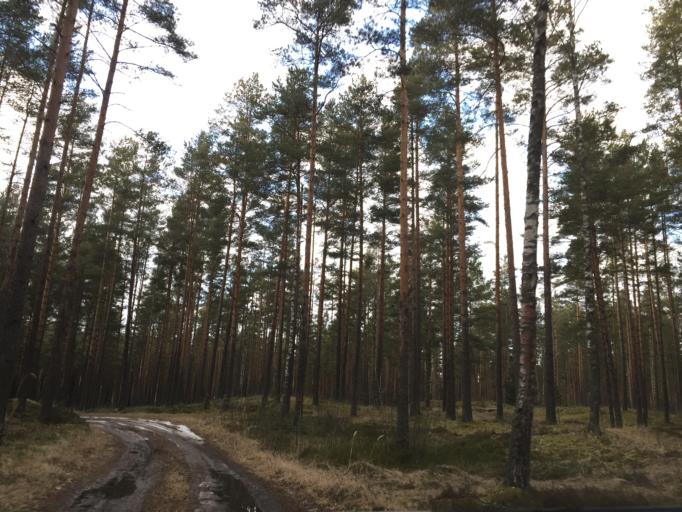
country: LV
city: Tireli
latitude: 56.8643
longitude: 23.6277
